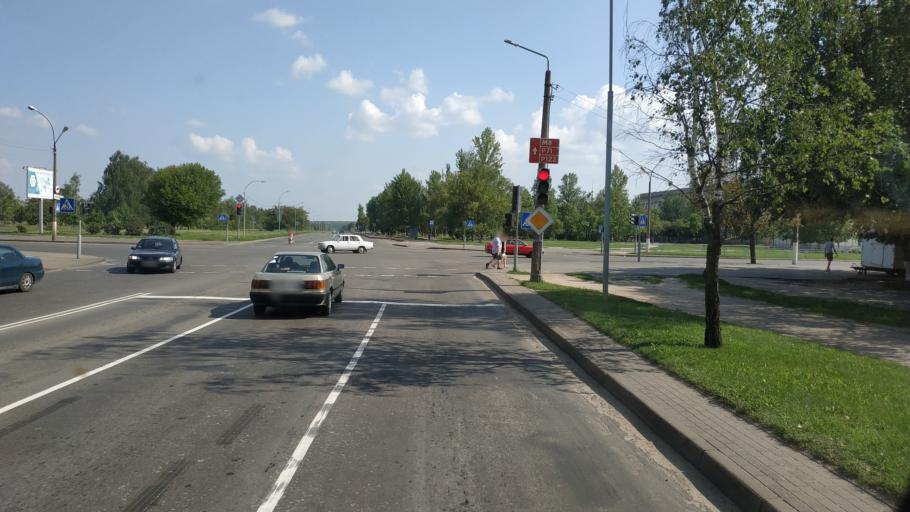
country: BY
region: Mogilev
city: Buynichy
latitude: 53.8667
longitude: 30.3151
